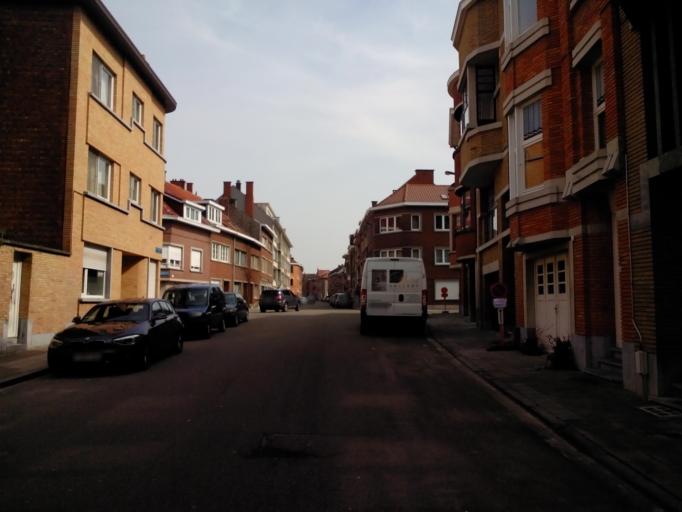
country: BE
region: Flanders
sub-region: Provincie Vlaams-Brabant
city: Leuven
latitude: 50.8694
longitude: 4.7021
